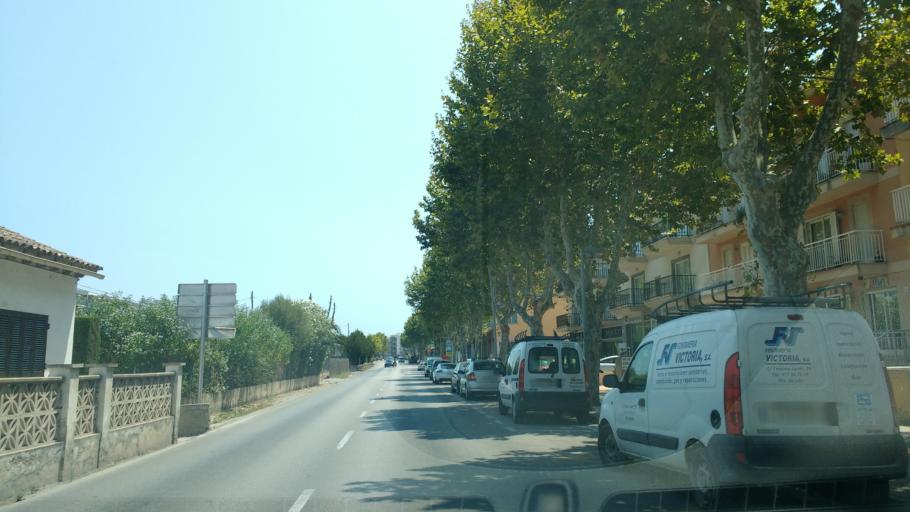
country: ES
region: Balearic Islands
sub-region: Illes Balears
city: Port d'Alcudia
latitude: 39.8453
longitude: 3.1318
